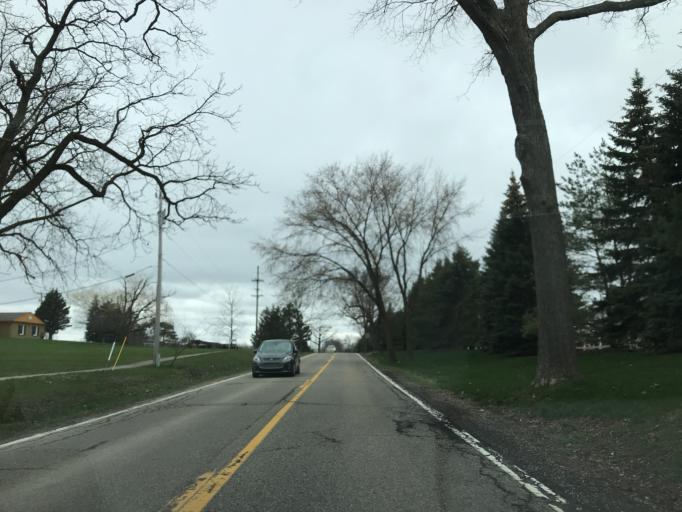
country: US
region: Michigan
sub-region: Oakland County
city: South Lyon
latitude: 42.4749
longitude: -83.6564
